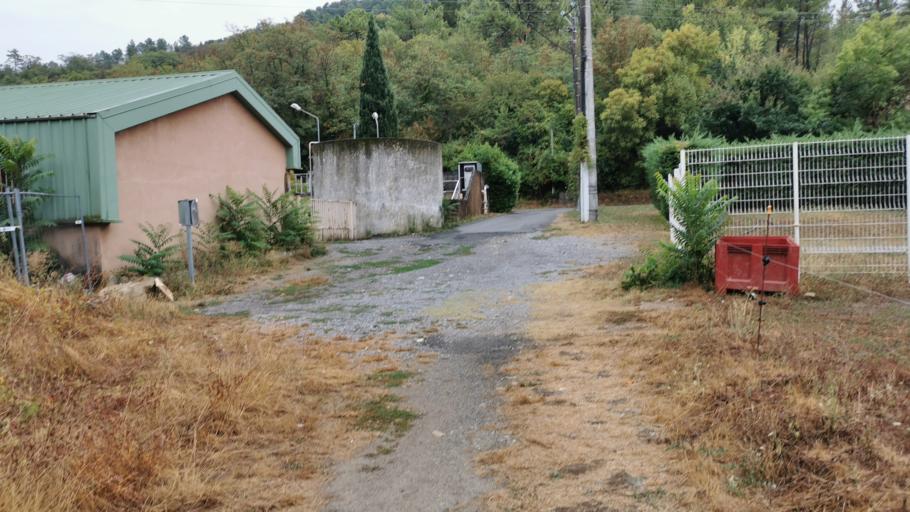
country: FR
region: Rhone-Alpes
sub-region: Departement de l'Ardeche
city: Les Vans
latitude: 44.4111
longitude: 4.1412
